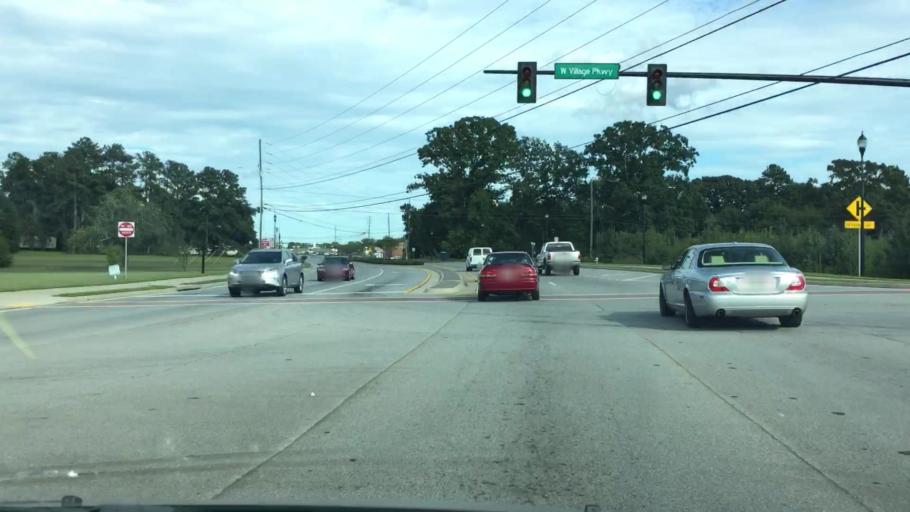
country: US
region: Georgia
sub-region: Henry County
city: Stockbridge
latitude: 33.6196
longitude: -84.2514
